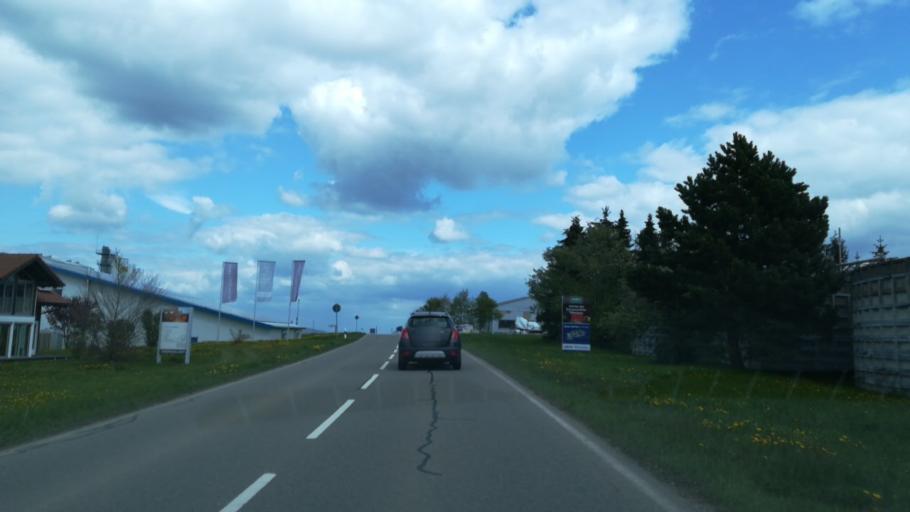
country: DE
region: Baden-Wuerttemberg
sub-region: Freiburg Region
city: Bonndorf im Schwarzwald
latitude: 47.8210
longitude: 8.3518
